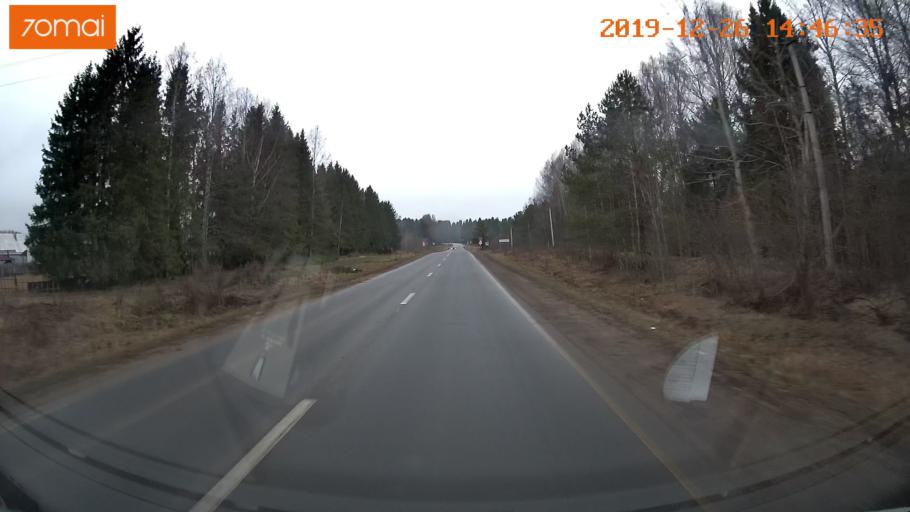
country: RU
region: Jaroslavl
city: Poshekhon'ye
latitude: 58.3374
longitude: 39.0150
